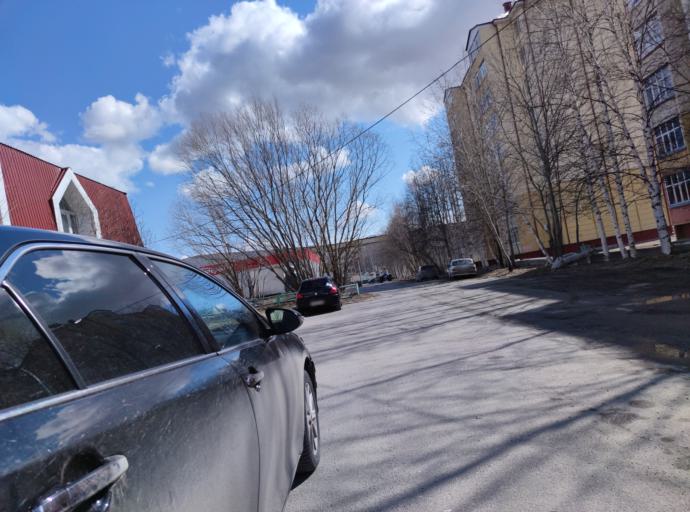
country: RU
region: Khanty-Mansiyskiy Avtonomnyy Okrug
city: Langepas
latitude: 61.2527
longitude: 75.1725
